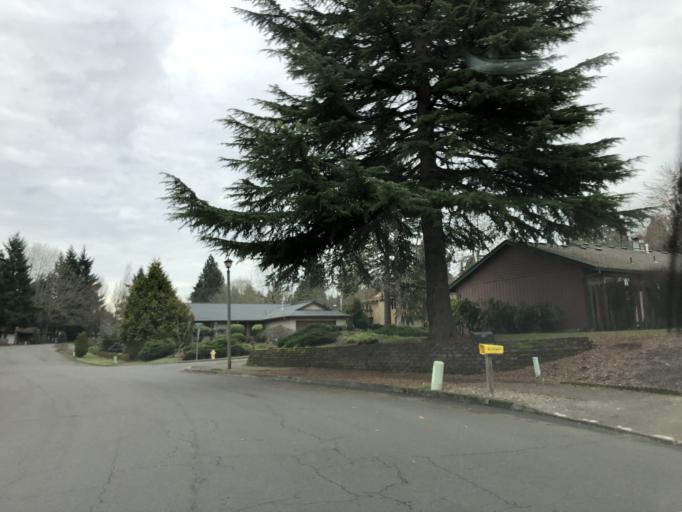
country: US
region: Oregon
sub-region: Washington County
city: Tigard
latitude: 45.4216
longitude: -122.7811
